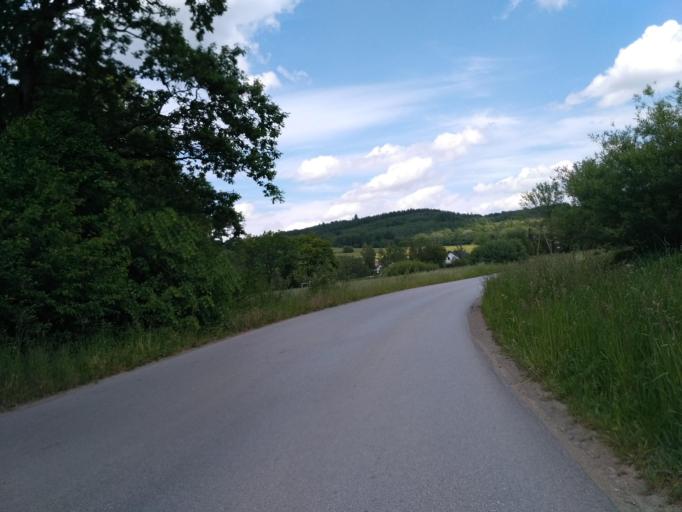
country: PL
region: Subcarpathian Voivodeship
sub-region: Powiat krosnienski
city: Chorkowka
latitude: 49.6058
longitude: 21.6220
